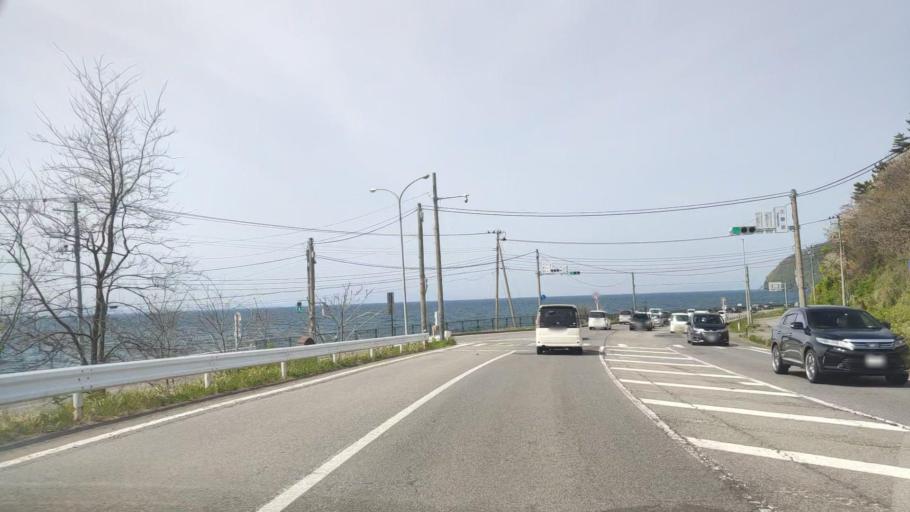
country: JP
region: Aomori
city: Aomori Shi
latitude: 40.8771
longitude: 140.8502
